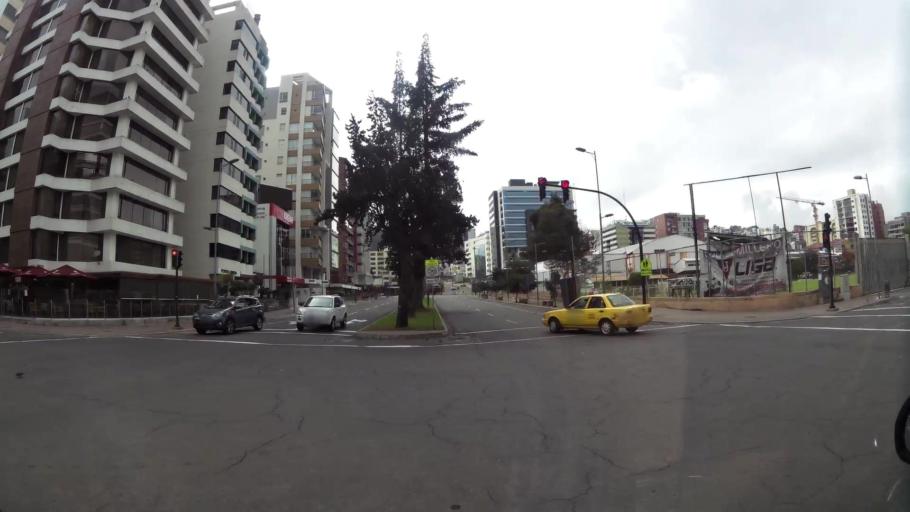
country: EC
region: Pichincha
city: Quito
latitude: -0.1819
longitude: -78.4803
